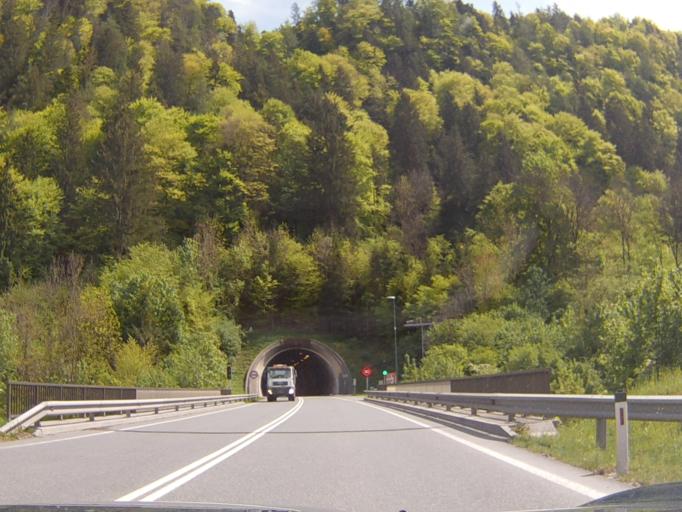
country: AT
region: Tyrol
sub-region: Politischer Bezirk Schwaz
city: Strass im Zillertal
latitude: 47.3937
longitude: 11.8112
